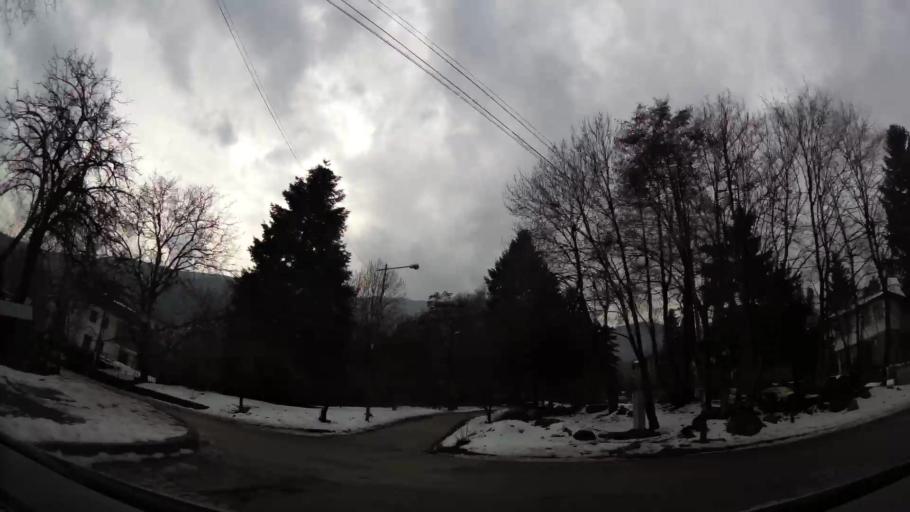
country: BG
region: Sofia-Capital
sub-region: Stolichna Obshtina
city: Sofia
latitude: 42.6456
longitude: 23.2679
